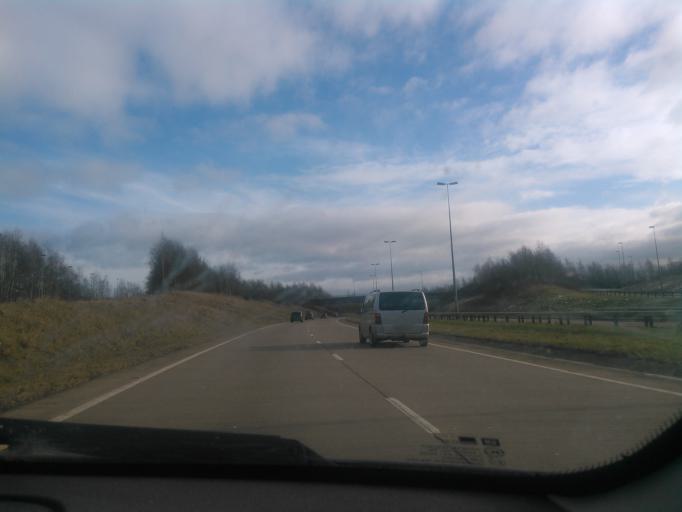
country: GB
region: England
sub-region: Staffordshire
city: Uttoxeter
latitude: 52.9102
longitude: -1.8265
